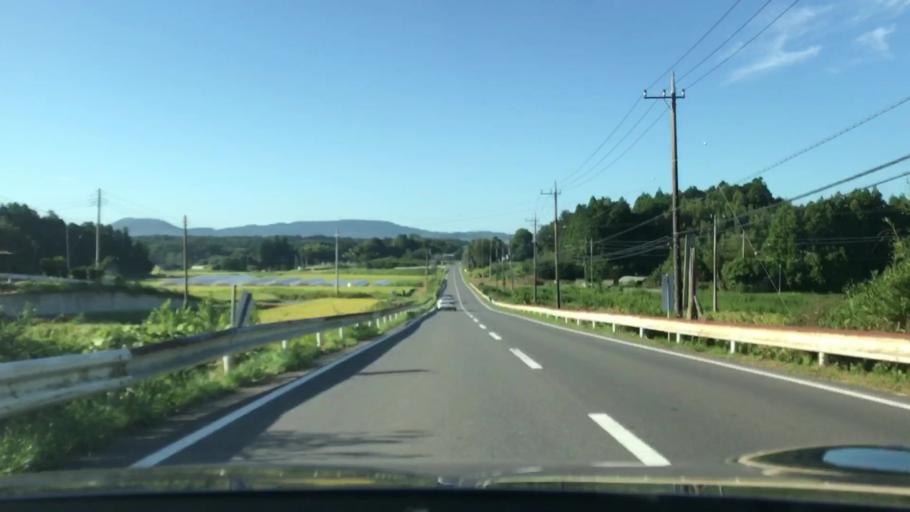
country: JP
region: Ibaraki
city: Makabe
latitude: 36.2483
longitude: 140.1649
